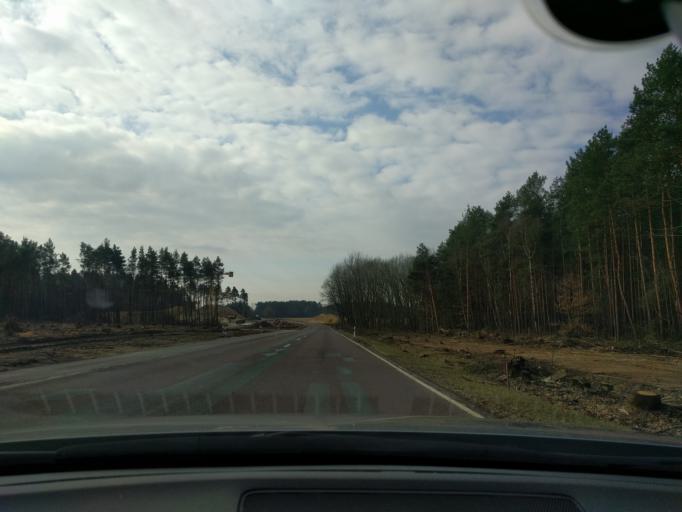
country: DE
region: Saxony-Anhalt
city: Colbitz
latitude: 52.3513
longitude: 11.6086
